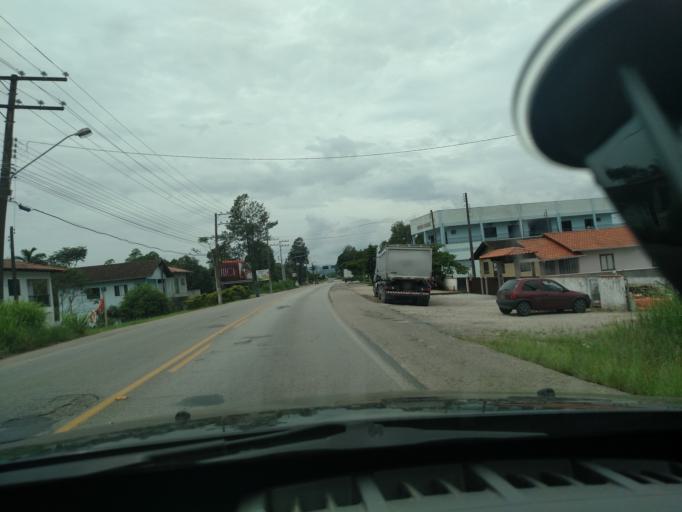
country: BR
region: Santa Catarina
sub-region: Gaspar
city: Gaspar
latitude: -26.9097
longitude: -48.9312
